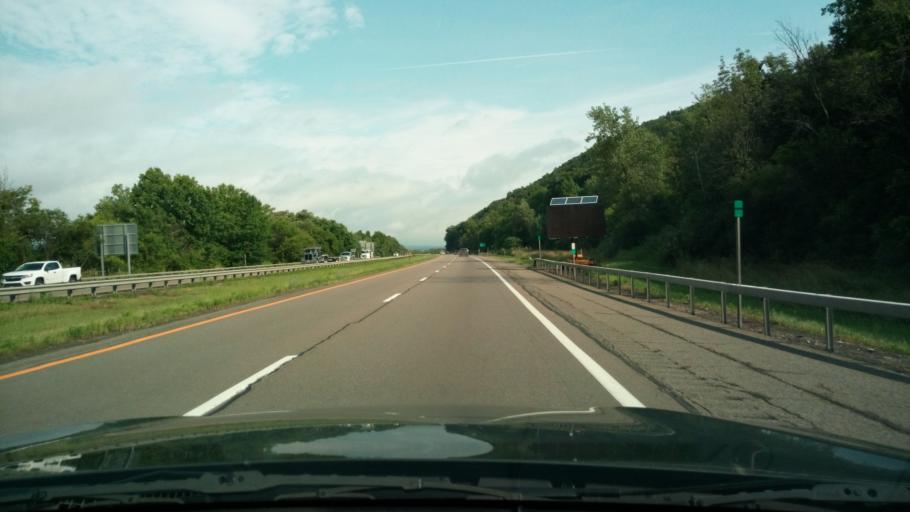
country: US
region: New York
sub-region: Chemung County
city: Elmira
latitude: 42.1120
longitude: -76.7973
